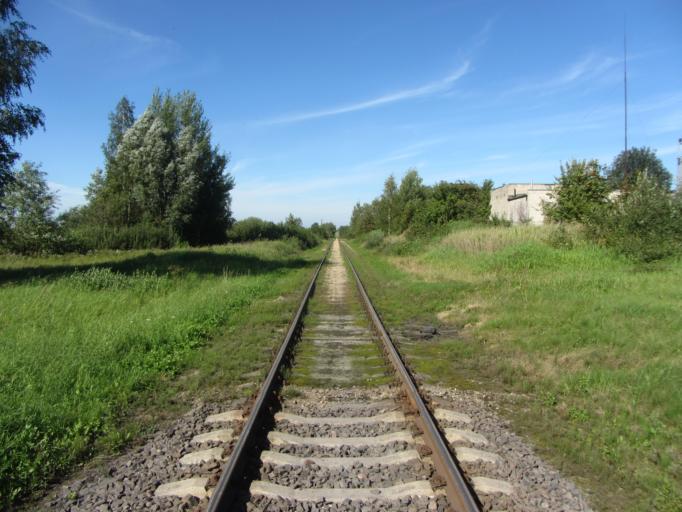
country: LT
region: Alytaus apskritis
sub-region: Alytus
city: Alytus
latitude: 54.4102
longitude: 24.0021
